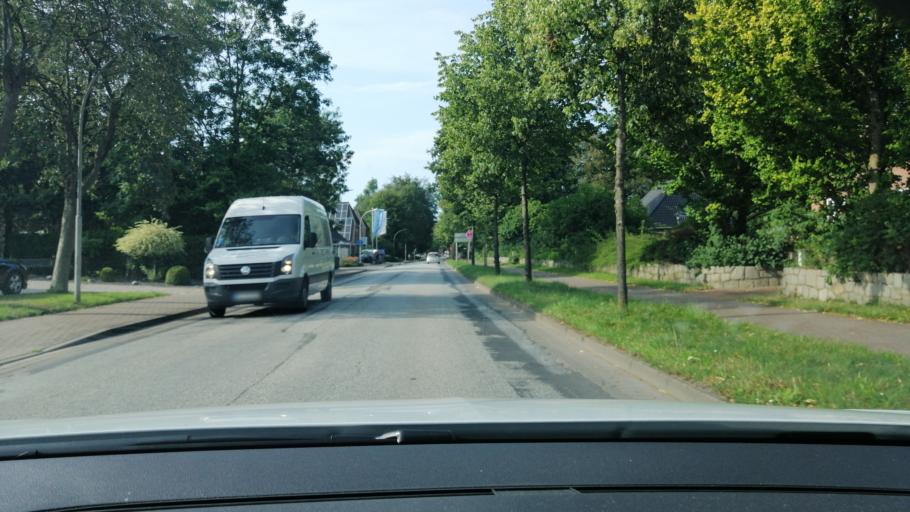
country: DE
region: Schleswig-Holstein
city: Leck
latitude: 54.7669
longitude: 8.9780
